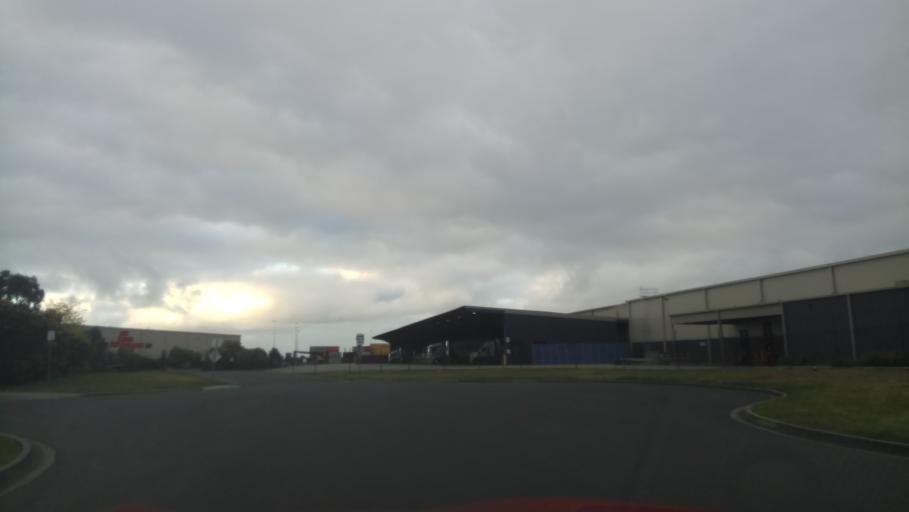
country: AU
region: Victoria
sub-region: Hobsons Bay
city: Laverton
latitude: -37.8563
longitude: 144.7886
